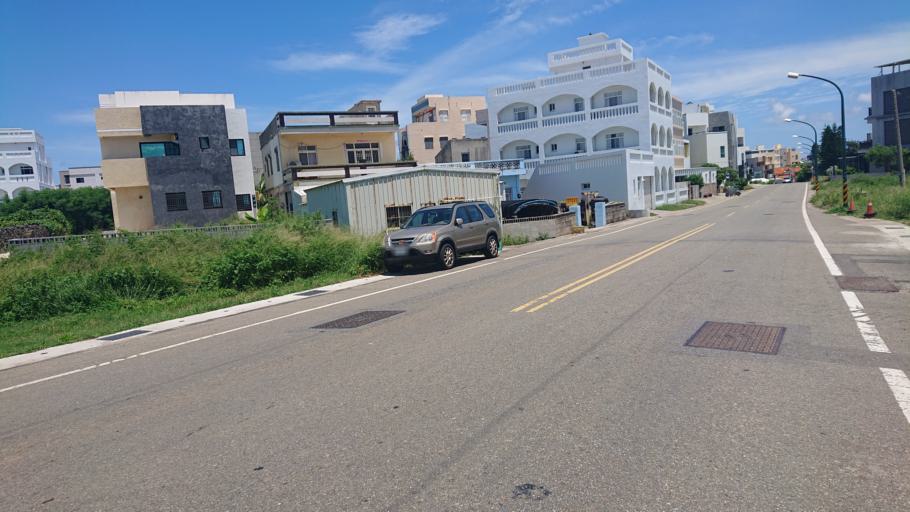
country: TW
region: Taiwan
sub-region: Penghu
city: Ma-kung
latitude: 23.5775
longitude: 119.5802
